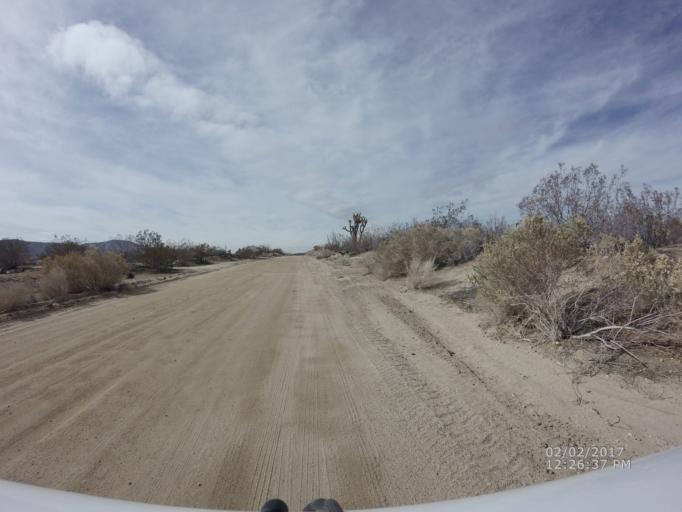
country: US
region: California
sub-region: Los Angeles County
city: Littlerock
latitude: 34.5138
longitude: -117.9878
